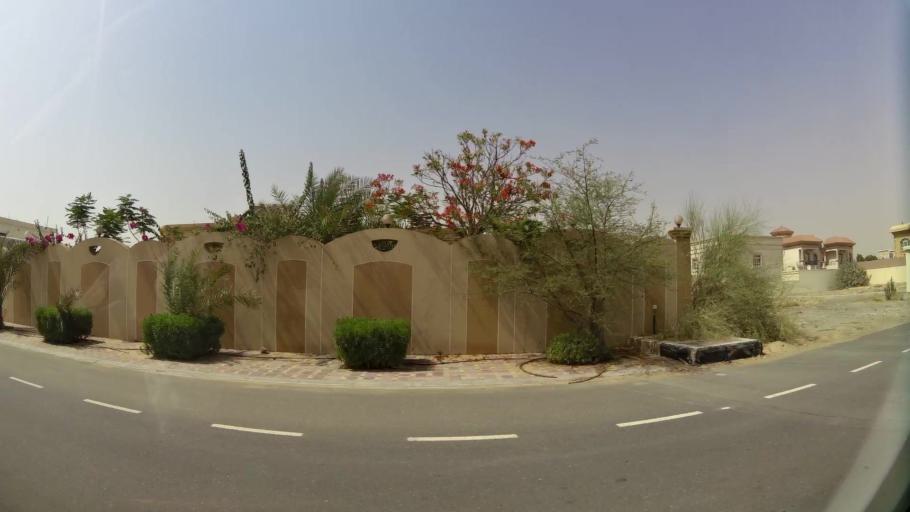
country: AE
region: Ash Shariqah
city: Sharjah
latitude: 25.2491
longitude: 55.4961
